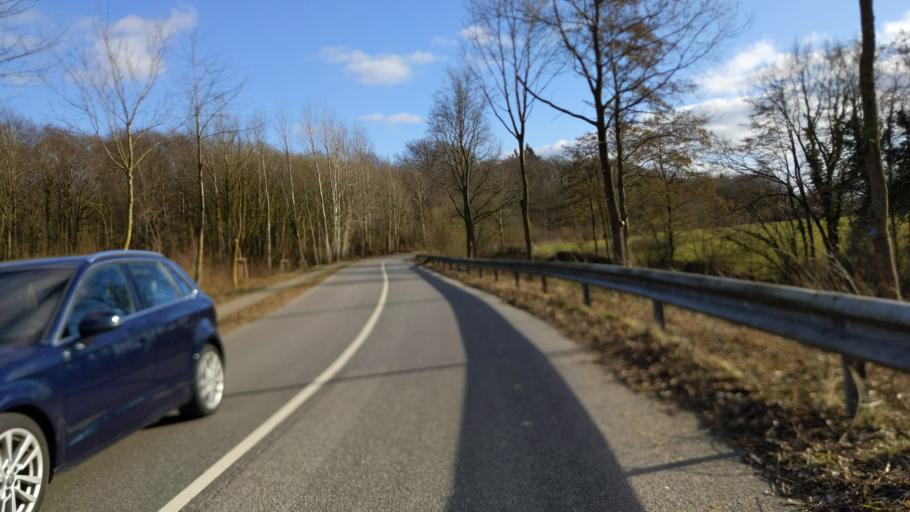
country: DE
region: Schleswig-Holstein
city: Timmendorfer Strand
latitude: 54.0068
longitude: 10.7535
